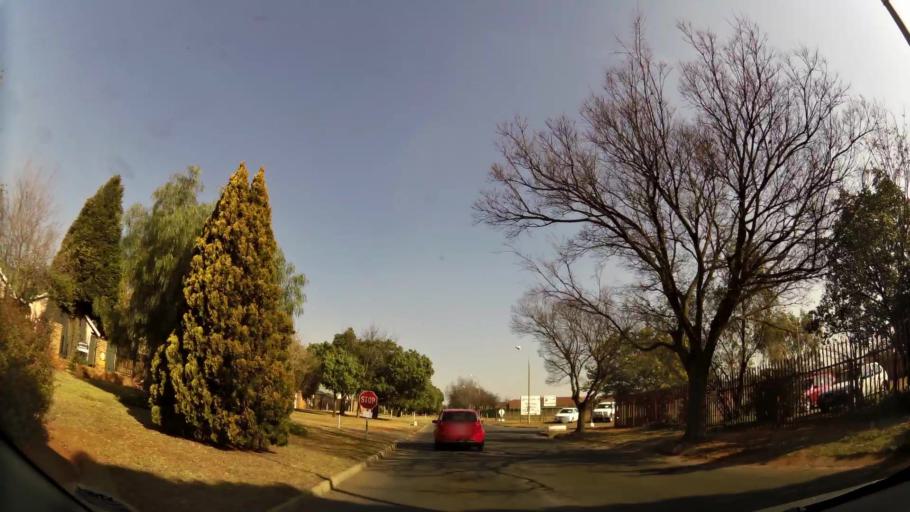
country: ZA
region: Gauteng
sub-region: West Rand District Municipality
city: Randfontein
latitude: -26.1782
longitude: 27.6874
